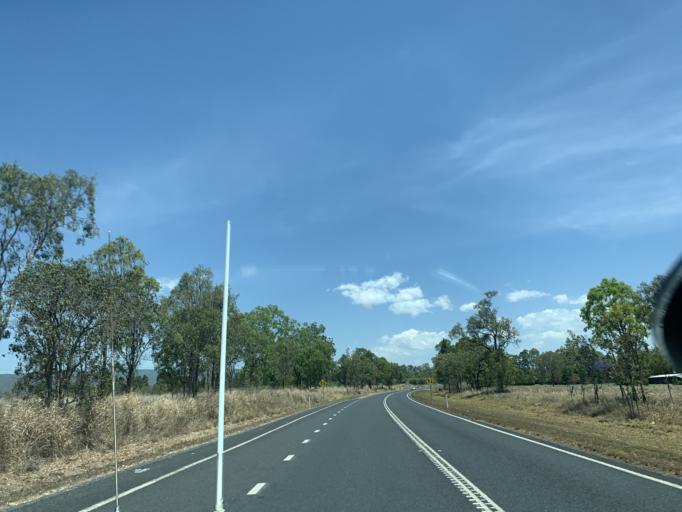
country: AU
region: Queensland
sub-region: Tablelands
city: Mareeba
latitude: -16.9723
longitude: 145.5343
